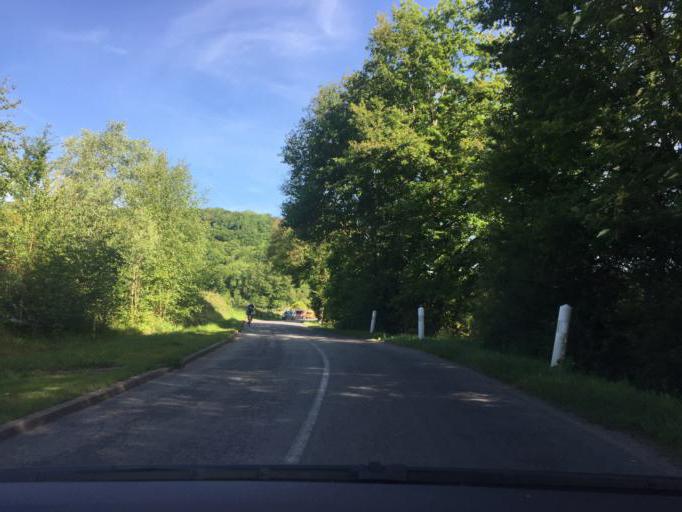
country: FR
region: Ile-de-France
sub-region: Departement de l'Essonne
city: Villiers-le-Bacle
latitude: 48.7123
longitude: 2.1198
